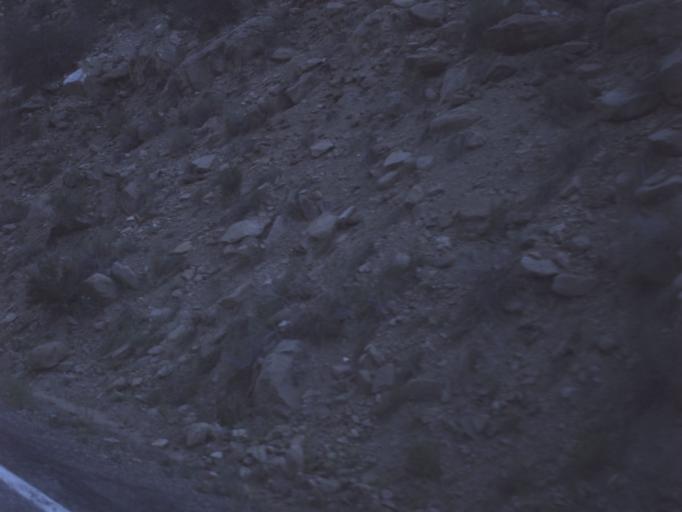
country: US
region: Utah
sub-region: Emery County
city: Huntington
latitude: 39.4639
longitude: -111.1457
